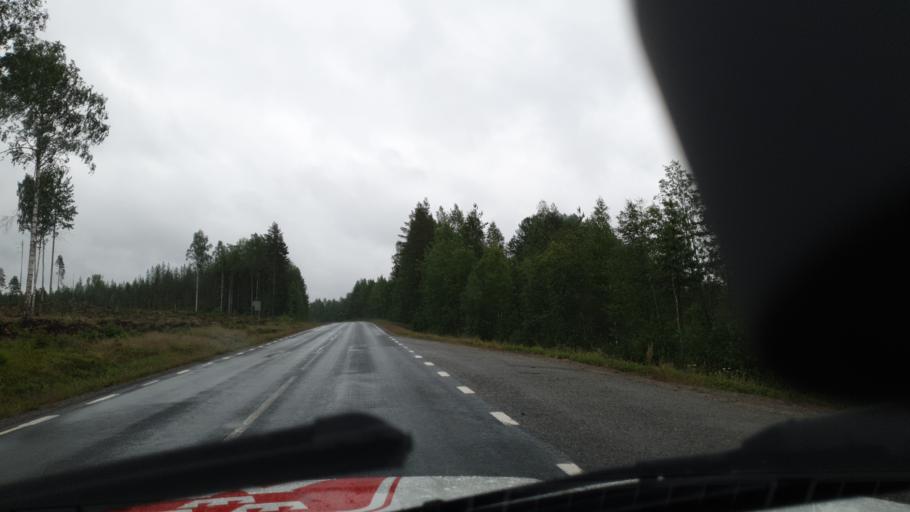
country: SE
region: Vaesterbotten
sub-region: Vannas Kommun
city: Vaennaes
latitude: 63.7714
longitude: 19.7041
